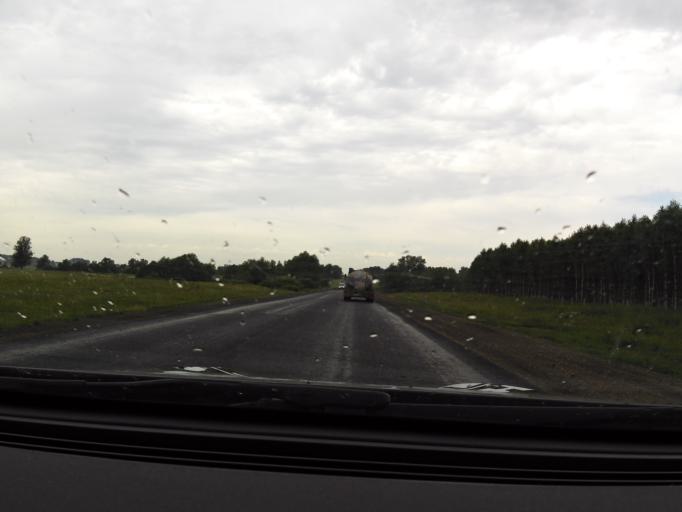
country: RU
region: Bashkortostan
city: Iglino
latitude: 54.7891
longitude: 56.5519
